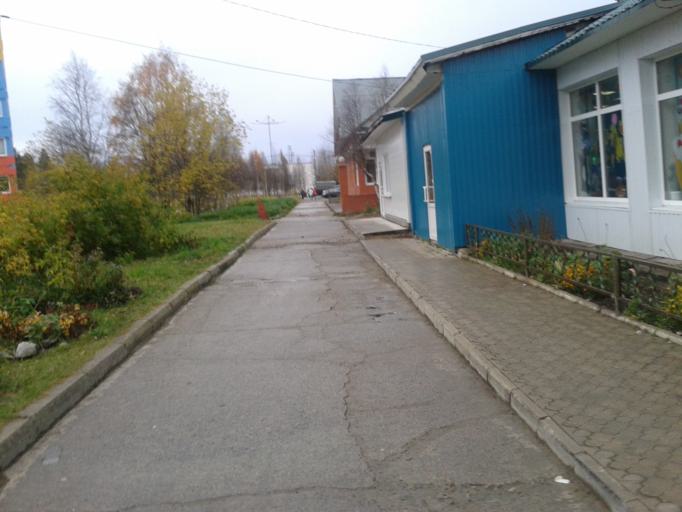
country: RU
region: Murmansk
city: Polyarnyye Zori
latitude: 67.3717
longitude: 32.4904
